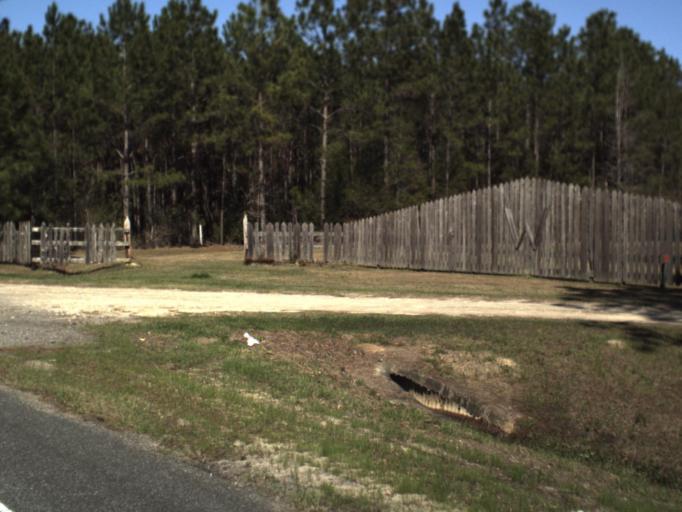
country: US
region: Florida
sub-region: Calhoun County
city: Blountstown
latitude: 30.3982
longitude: -85.0866
